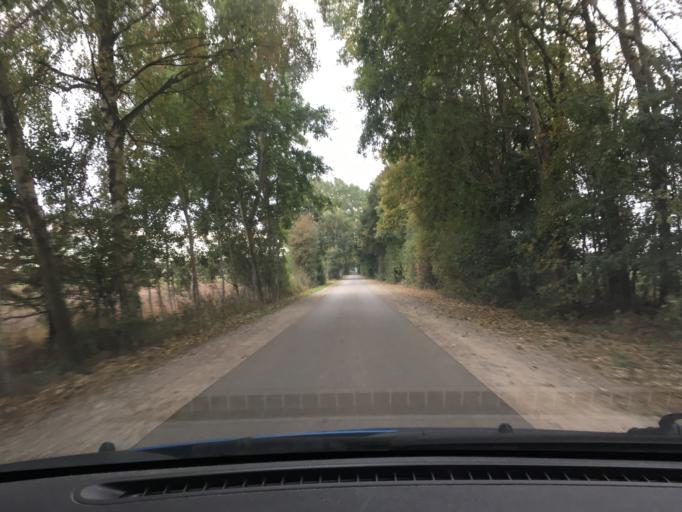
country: DE
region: Lower Saxony
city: Winsen
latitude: 53.3627
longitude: 10.2349
